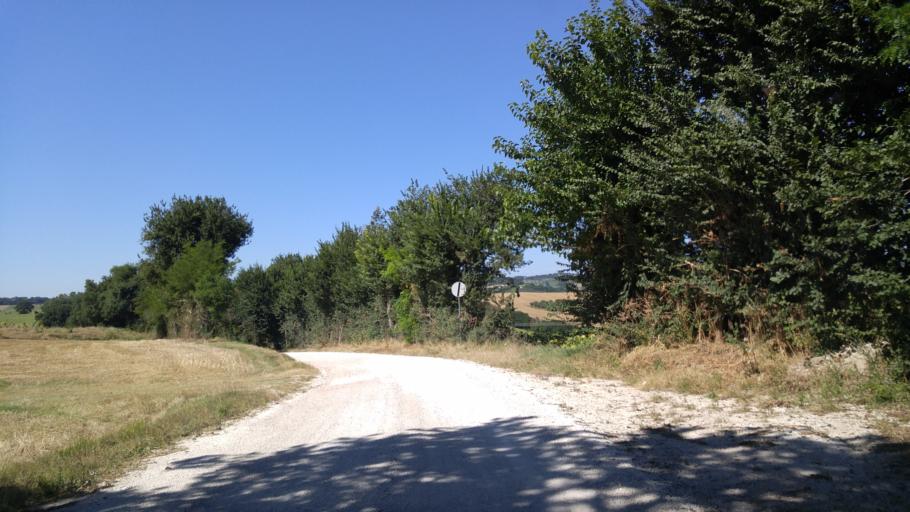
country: IT
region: The Marches
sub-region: Provincia di Pesaro e Urbino
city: Mombaroccio
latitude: 43.8259
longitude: 12.8899
